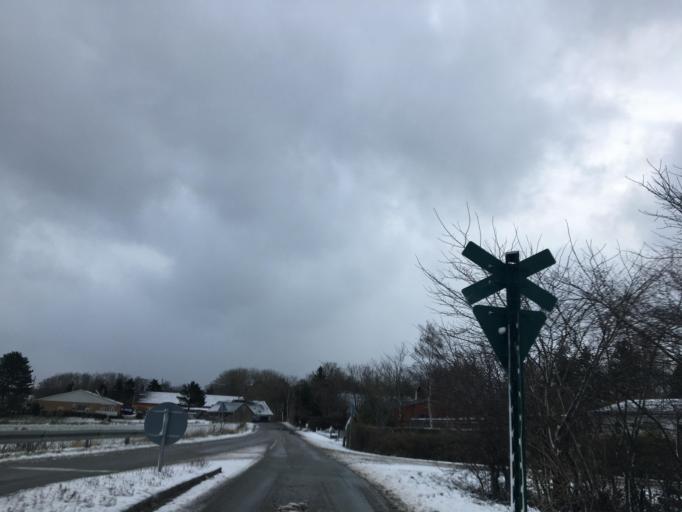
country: DK
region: Zealand
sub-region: Odsherred Kommune
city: Asnaes
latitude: 55.8311
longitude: 11.5634
